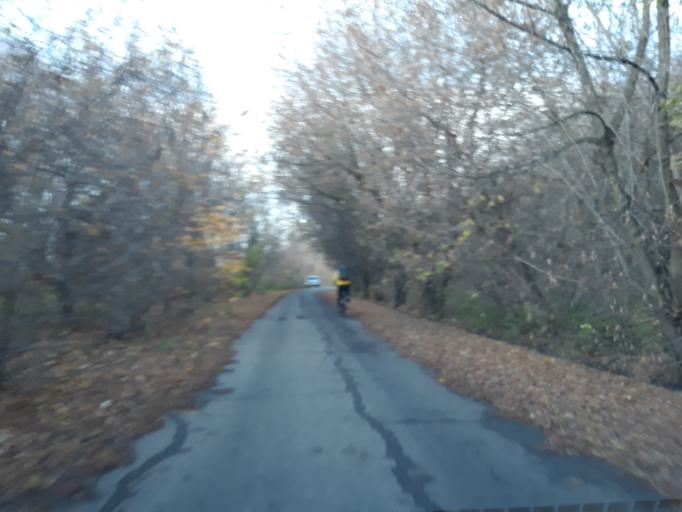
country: RU
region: Nizjnij Novgorod
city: Nizhniy Novgorod
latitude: 56.2807
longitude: 43.9696
